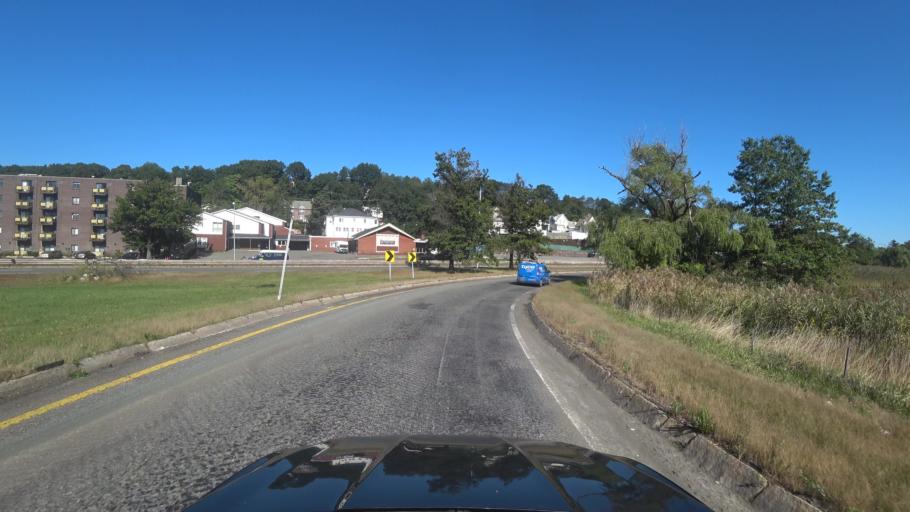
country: US
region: Massachusetts
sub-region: Suffolk County
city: Revere
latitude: 42.4062
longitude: -71.0245
